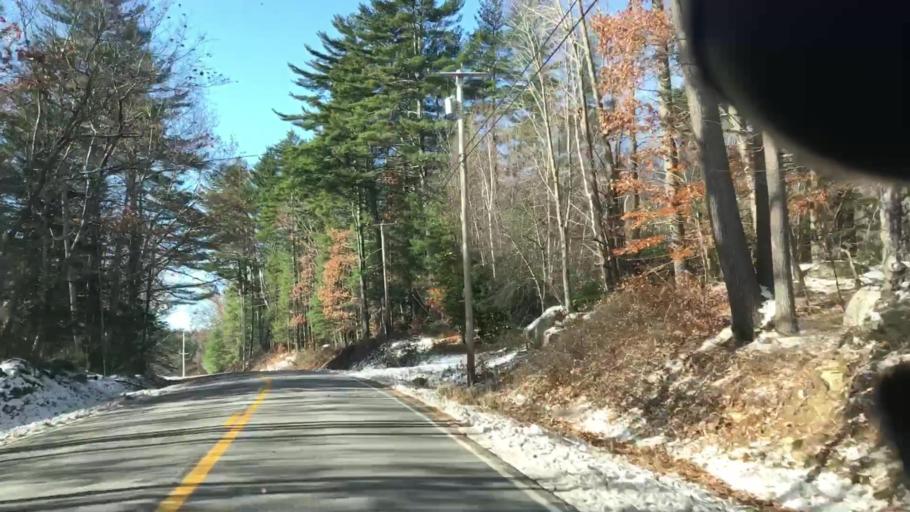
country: US
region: Maine
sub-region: Oxford County
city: Denmark
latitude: 43.9704
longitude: -70.8178
